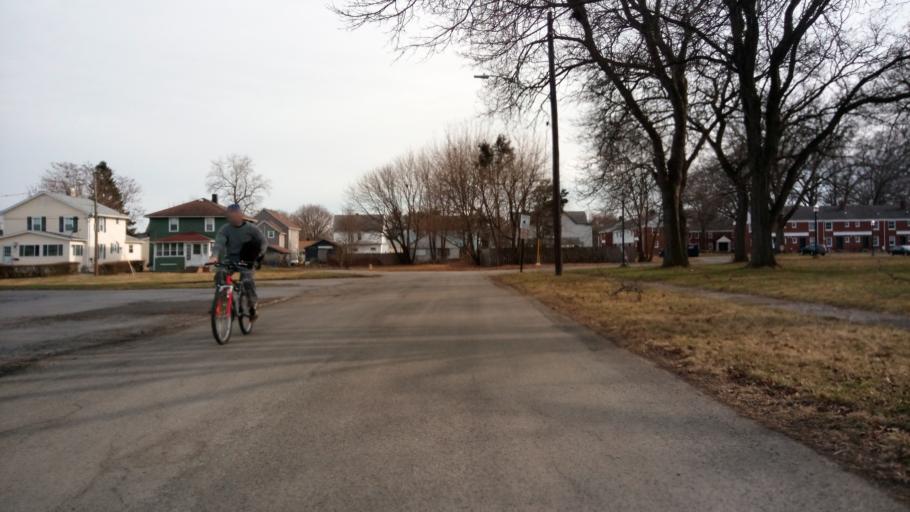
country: US
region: New York
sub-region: Chemung County
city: Elmira Heights
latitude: 42.1109
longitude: -76.8216
